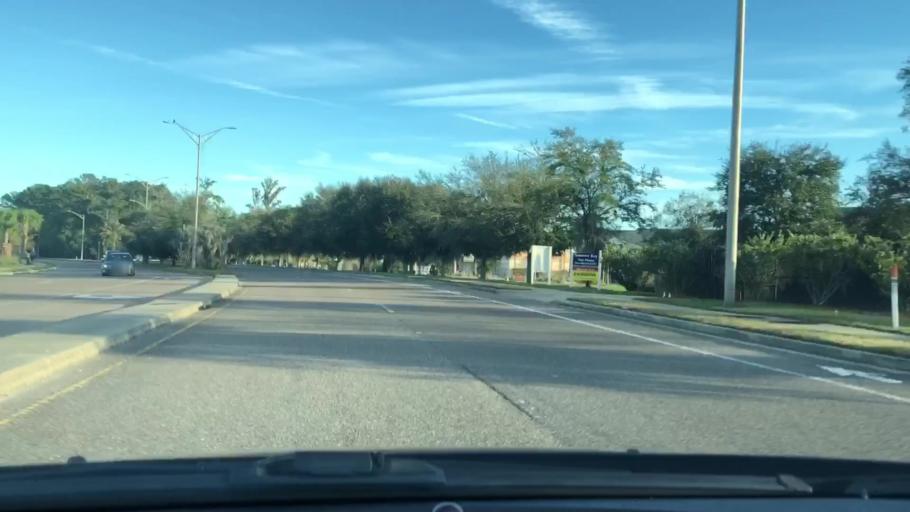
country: US
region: Florida
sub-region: Duval County
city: Jacksonville
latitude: 30.2476
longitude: -81.5612
